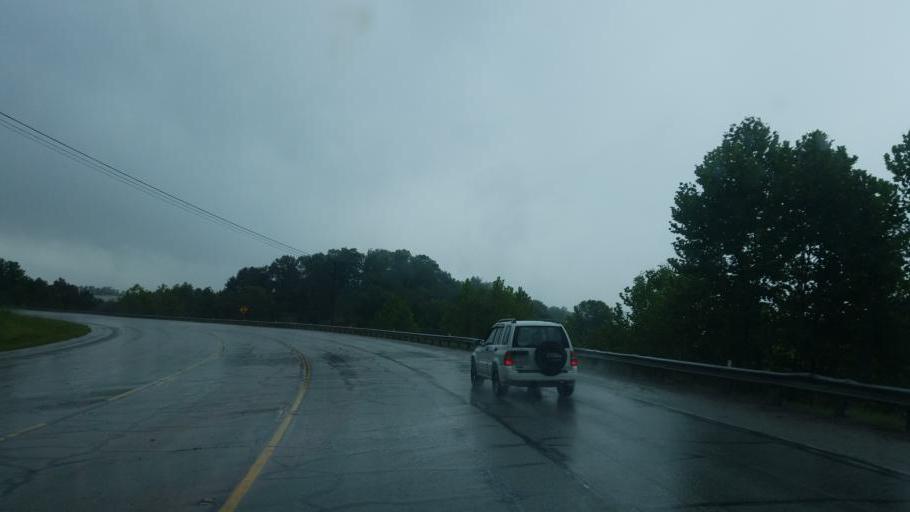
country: US
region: Kentucky
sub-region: Rowan County
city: Morehead
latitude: 38.1974
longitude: -83.4820
